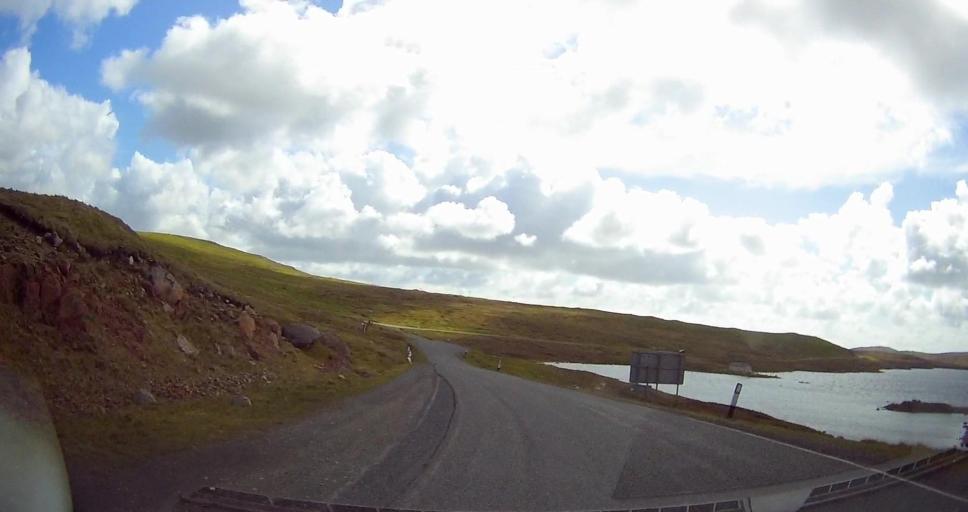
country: GB
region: Scotland
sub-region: Shetland Islands
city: Lerwick
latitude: 60.4893
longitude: -1.3900
